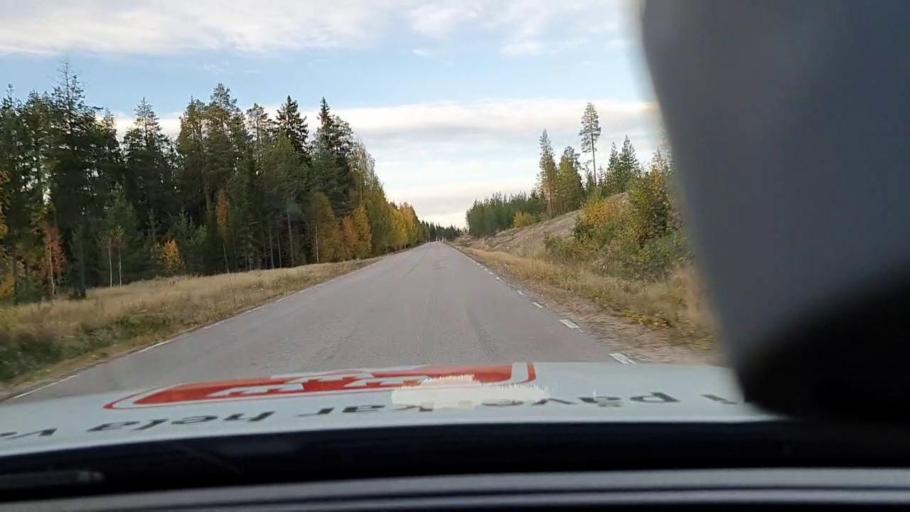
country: SE
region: Norrbotten
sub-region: Overkalix Kommun
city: OEverkalix
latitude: 66.3260
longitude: 22.7700
